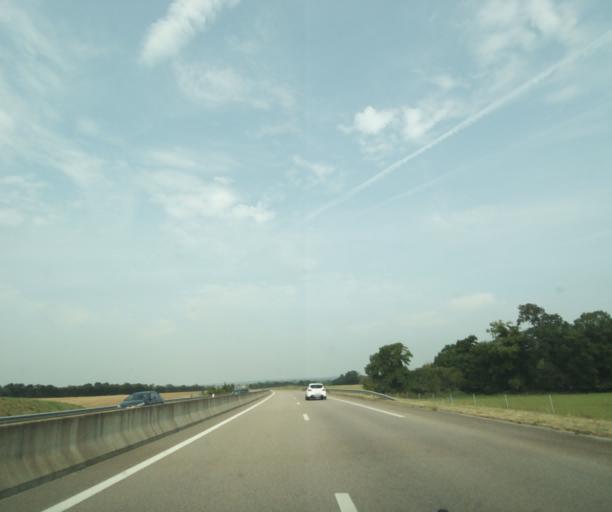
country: FR
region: Lower Normandy
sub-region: Departement du Calvados
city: Falaise
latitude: 48.8580
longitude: -0.1825
